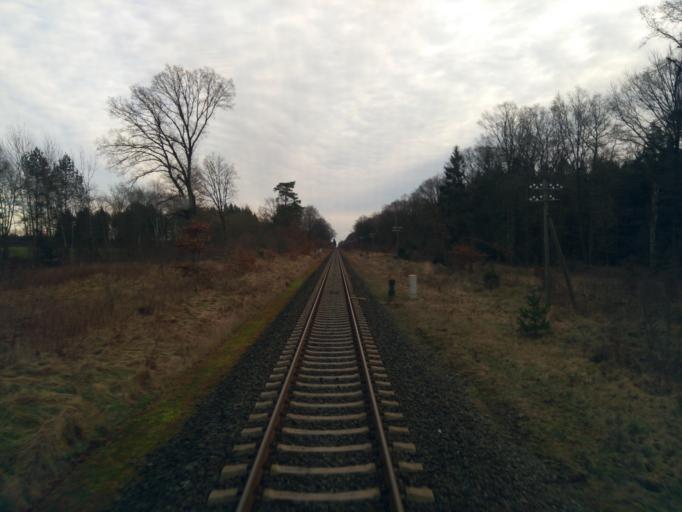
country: DE
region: Lower Saxony
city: Wriedel
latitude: 52.9993
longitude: 10.2271
